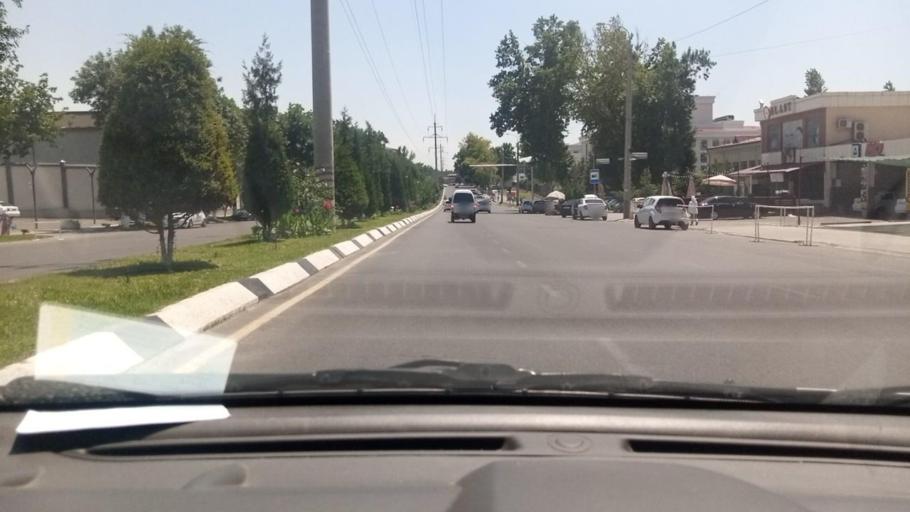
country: UZ
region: Toshkent Shahri
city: Tashkent
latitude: 41.2883
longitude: 69.1943
